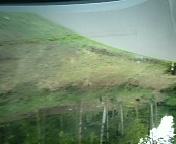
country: DE
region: Baden-Wuerttemberg
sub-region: Freiburg Region
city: Oppenau
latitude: 48.4265
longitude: 8.1580
